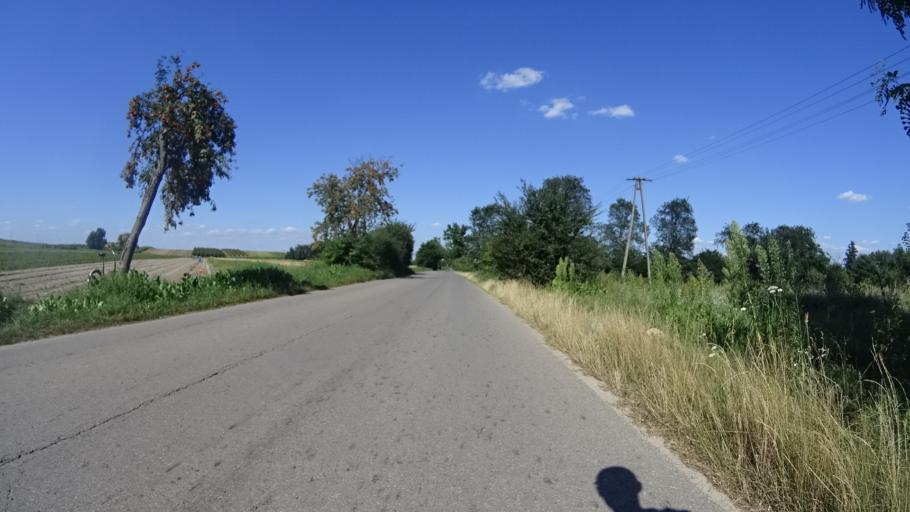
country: PL
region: Masovian Voivodeship
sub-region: Powiat bialobrzeski
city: Wysmierzyce
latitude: 51.6583
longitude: 20.8267
